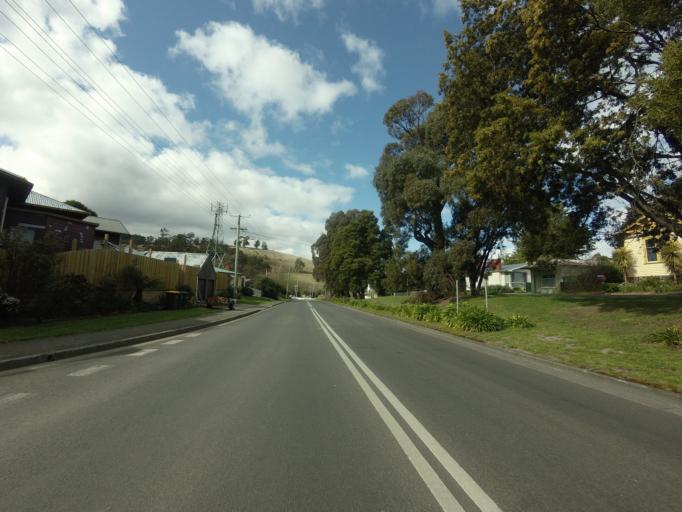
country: AU
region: Tasmania
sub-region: Huon Valley
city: Geeveston
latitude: -43.1645
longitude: 146.9272
